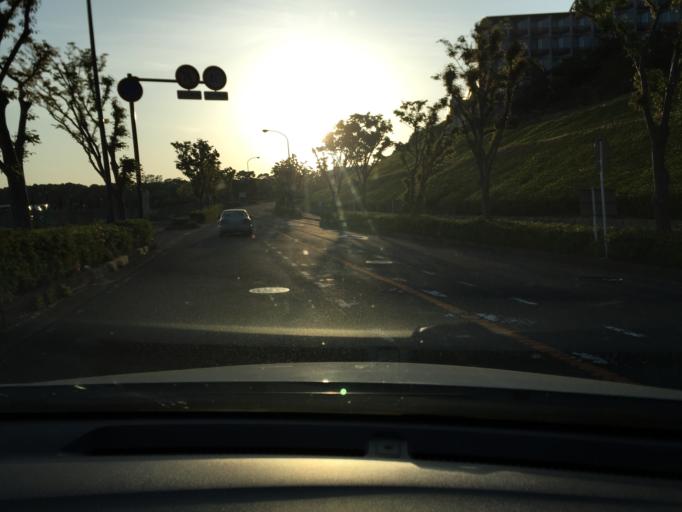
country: JP
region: Kanagawa
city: Hayama
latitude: 35.2540
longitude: 139.6080
